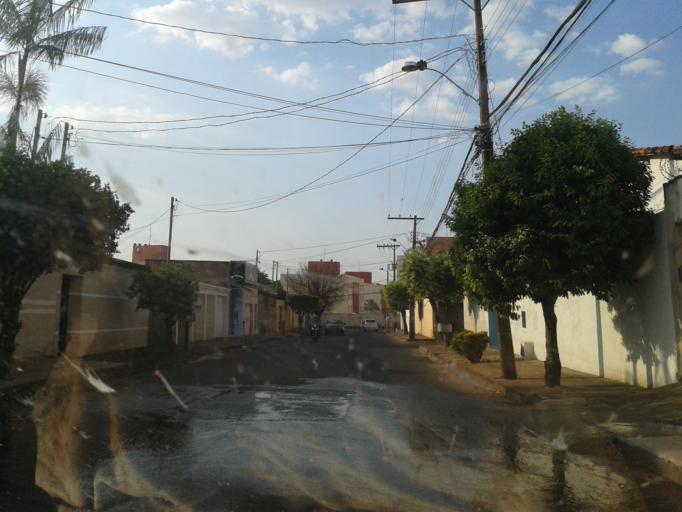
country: BR
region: Minas Gerais
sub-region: Uberlandia
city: Uberlandia
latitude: -18.9401
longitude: -48.3199
